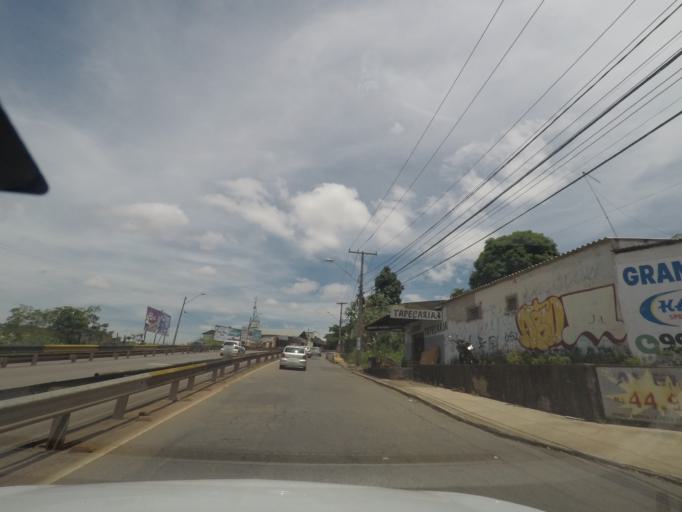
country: BR
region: Goias
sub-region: Goiania
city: Goiania
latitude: -16.6689
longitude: -49.2237
